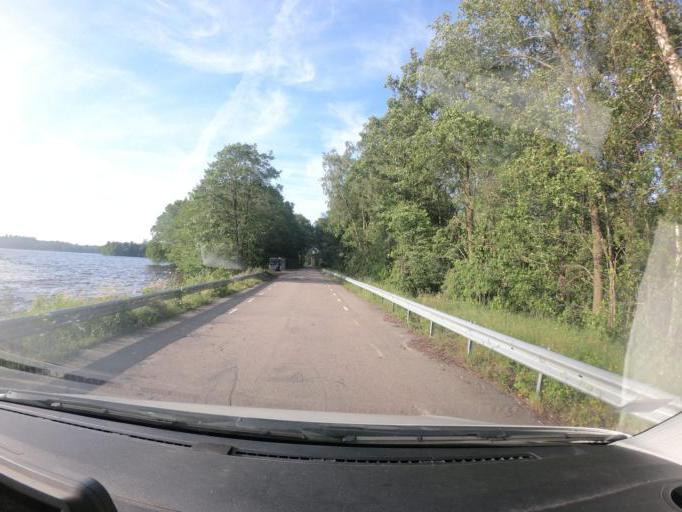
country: SE
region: Skane
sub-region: Angelholms Kommun
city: Munka-Ljungby
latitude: 56.3193
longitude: 13.0702
